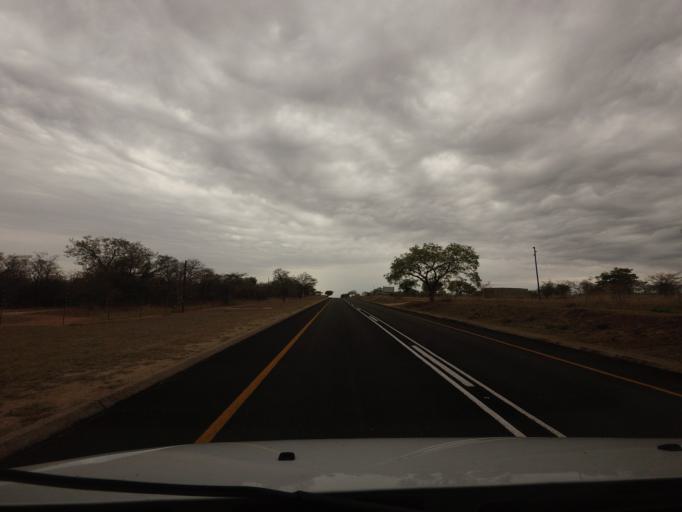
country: ZA
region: Limpopo
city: Thulamahashi
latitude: -24.5662
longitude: 31.1068
